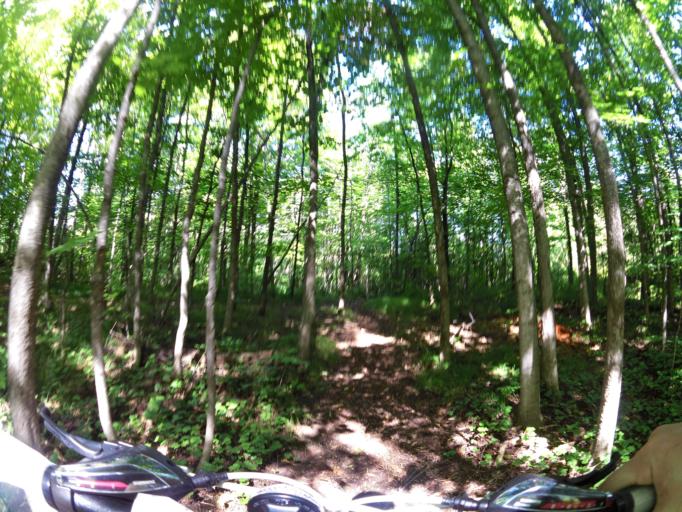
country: CA
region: Ontario
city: Bells Corners
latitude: 45.3224
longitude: -75.9002
